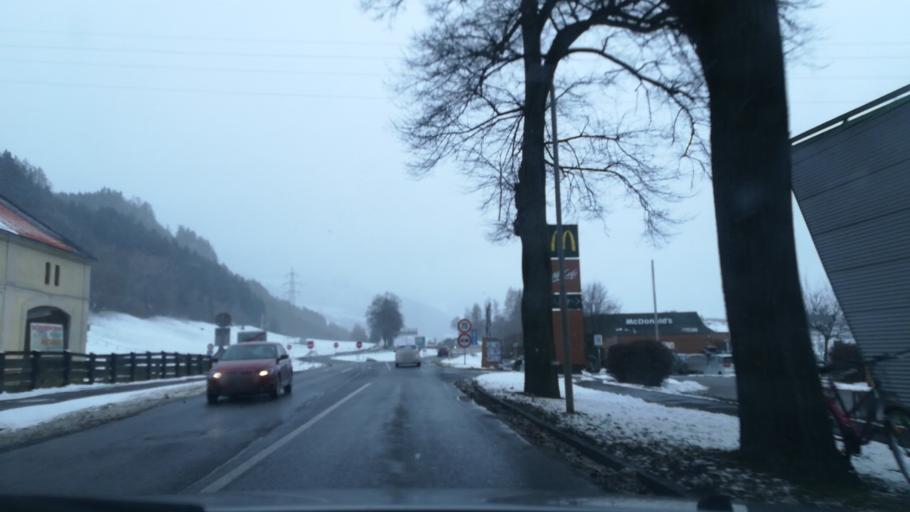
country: AT
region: Styria
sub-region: Politischer Bezirk Murtal
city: Oberweg
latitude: 47.1718
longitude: 14.6328
